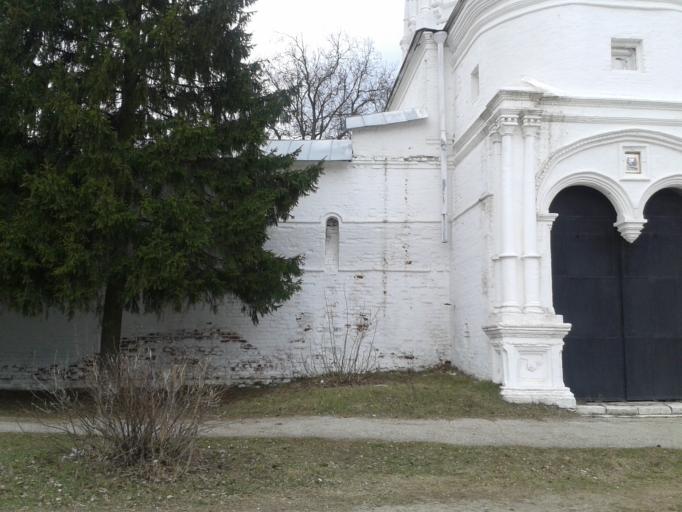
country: RU
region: Rjazan
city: Solotcha
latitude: 54.7908
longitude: 39.8344
